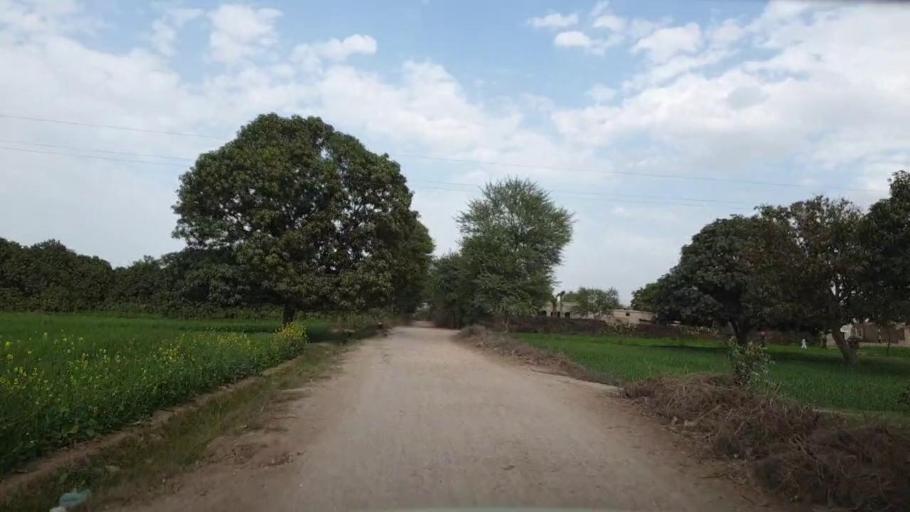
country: PK
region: Sindh
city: Matiari
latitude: 25.5626
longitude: 68.5678
